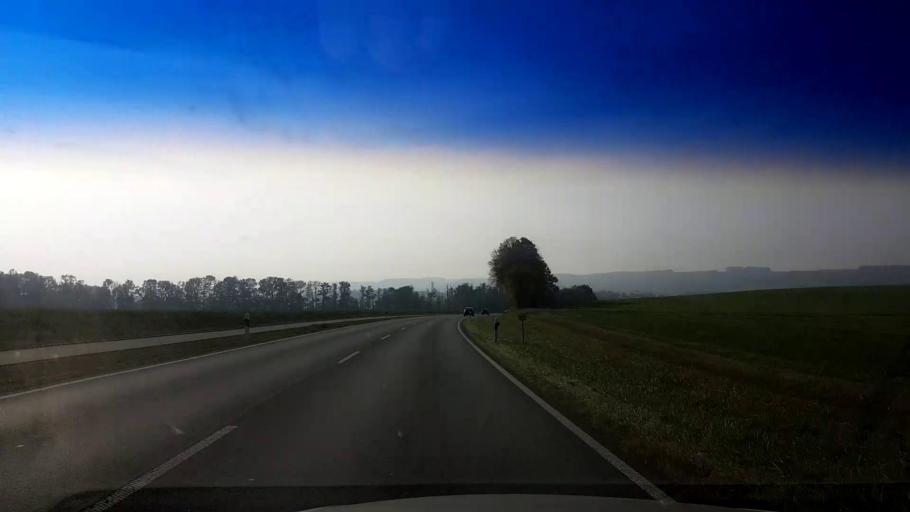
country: DE
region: Bavaria
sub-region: Upper Franconia
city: Himmelkron
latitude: 50.0749
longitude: 11.6097
